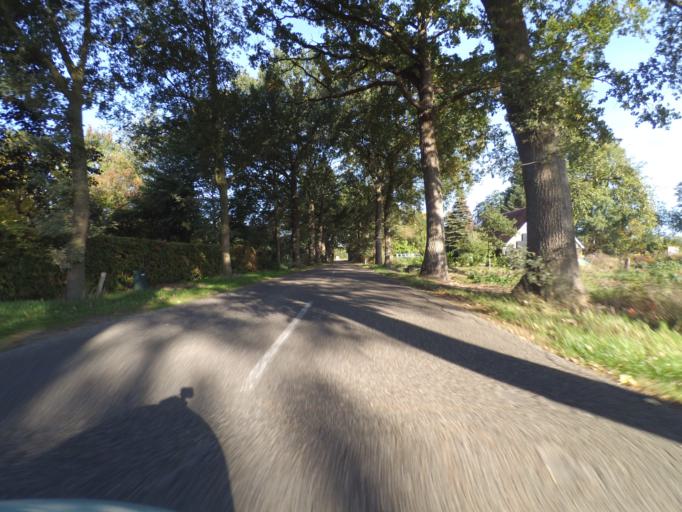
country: NL
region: Gelderland
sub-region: Berkelland
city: Eibergen
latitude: 52.0934
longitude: 6.6612
